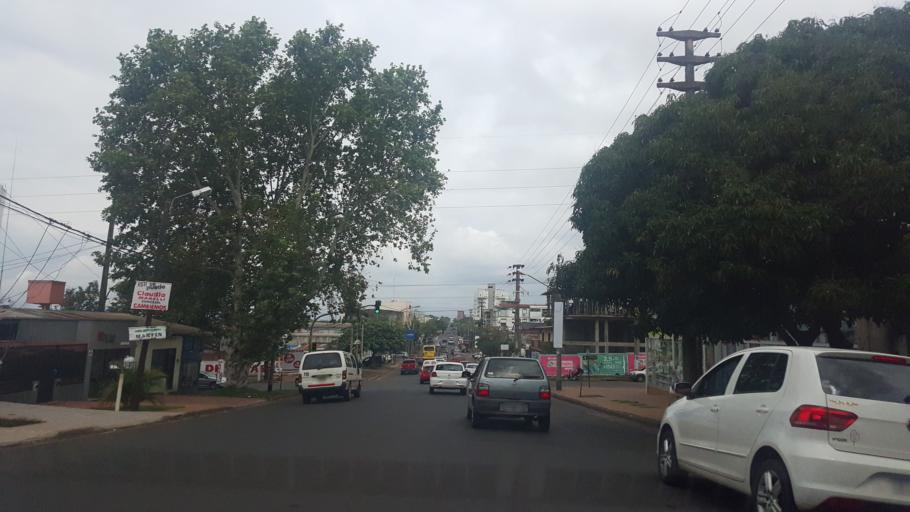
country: AR
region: Misiones
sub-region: Departamento de Capital
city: Posadas
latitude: -27.3767
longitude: -55.9027
